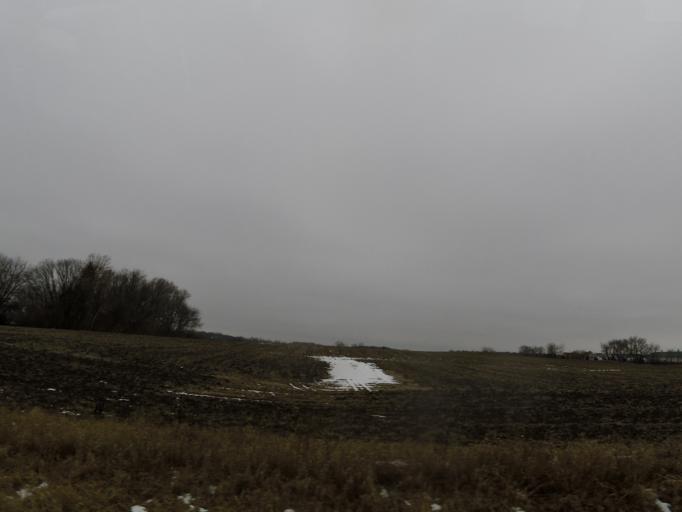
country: US
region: Minnesota
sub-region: Carver County
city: Watertown
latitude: 45.0093
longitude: -93.8487
